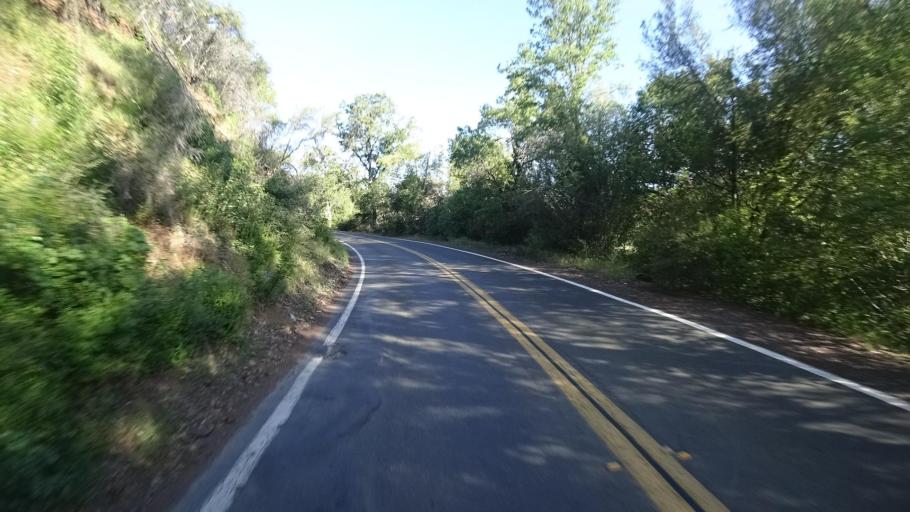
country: US
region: California
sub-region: Lake County
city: North Lakeport
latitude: 39.1122
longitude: -122.9797
